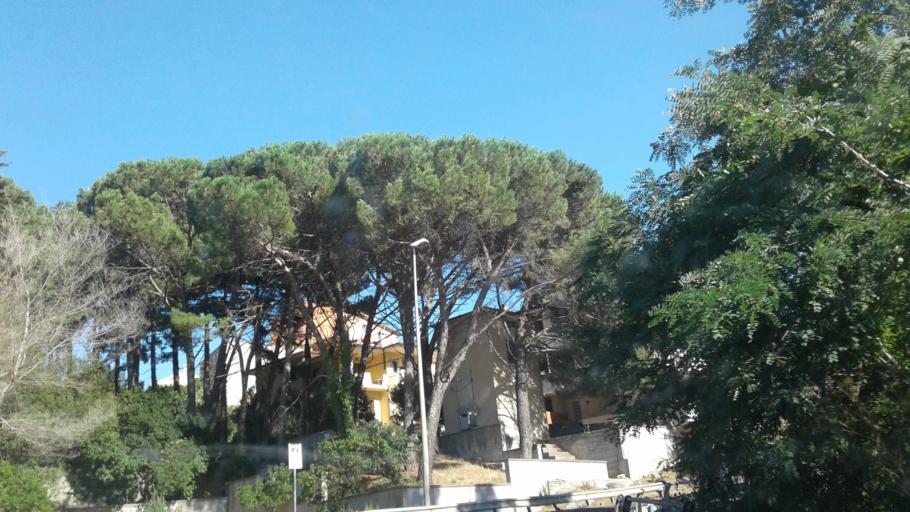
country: IT
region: Sardinia
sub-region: Provincia di Olbia-Tempio
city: Tempio Pausania
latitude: 40.9068
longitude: 9.0954
